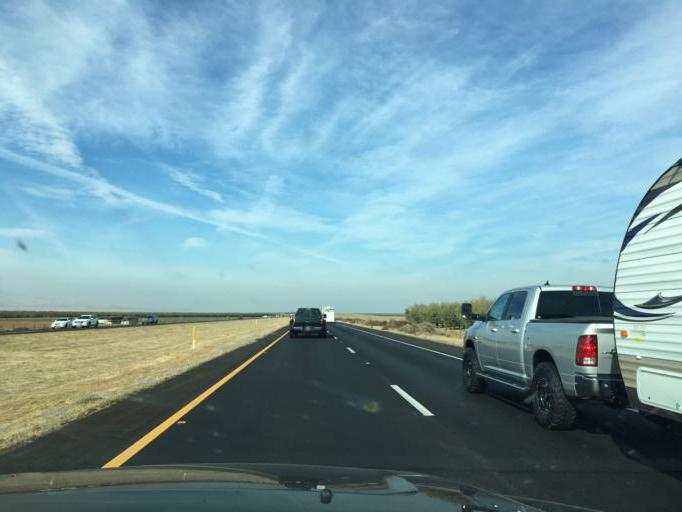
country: US
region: California
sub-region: Fresno County
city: Huron
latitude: 36.1936
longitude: -120.2056
